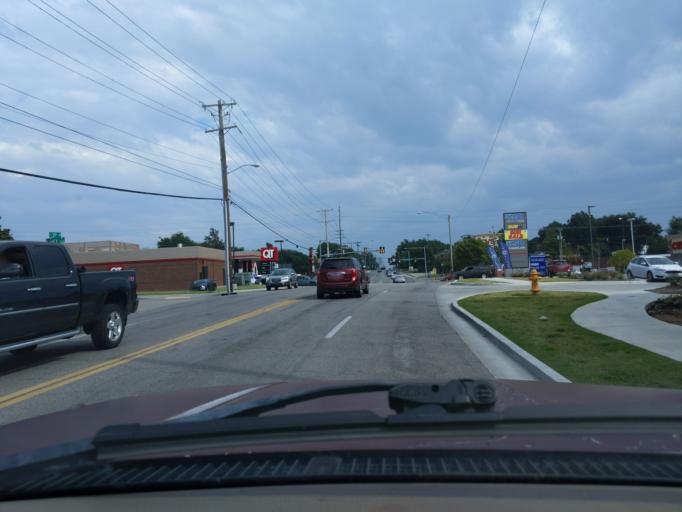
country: US
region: Oklahoma
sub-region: Tulsa County
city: Tulsa
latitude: 36.1333
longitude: -95.9418
